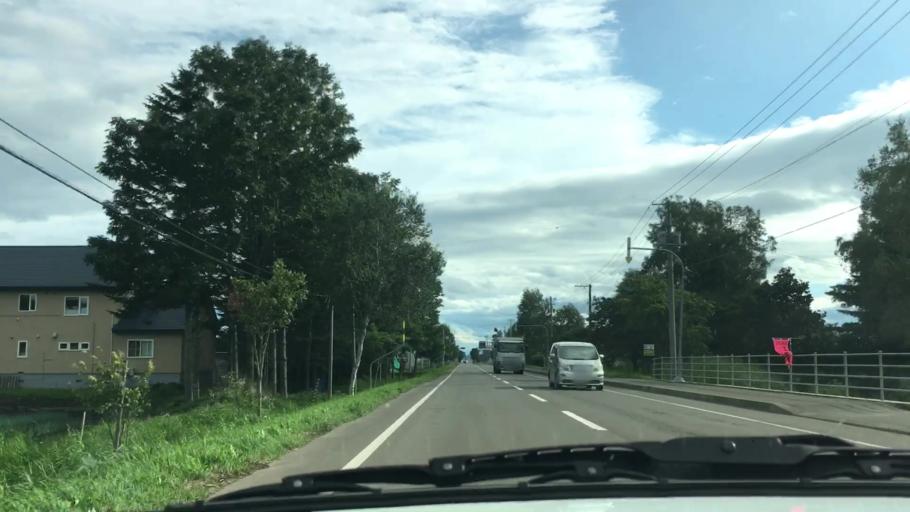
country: JP
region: Hokkaido
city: Otofuke
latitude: 43.2431
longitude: 143.2974
